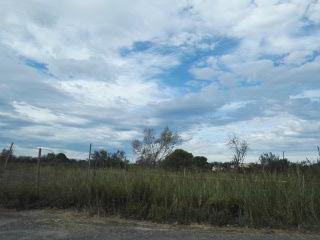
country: FR
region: Languedoc-Roussillon
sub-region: Departement de l'Herault
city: Le Cap d'Agde
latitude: 43.3128
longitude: 3.5406
